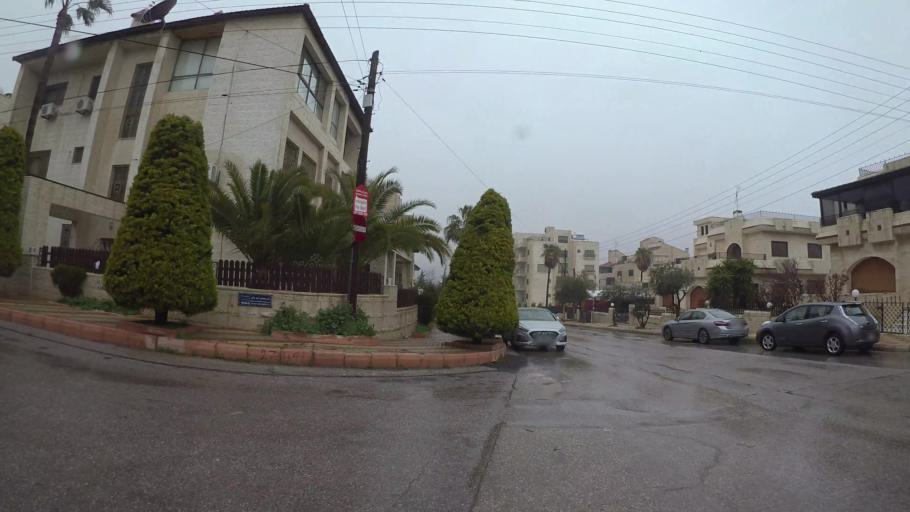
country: JO
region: Amman
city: Wadi as Sir
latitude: 31.9648
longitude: 35.8700
